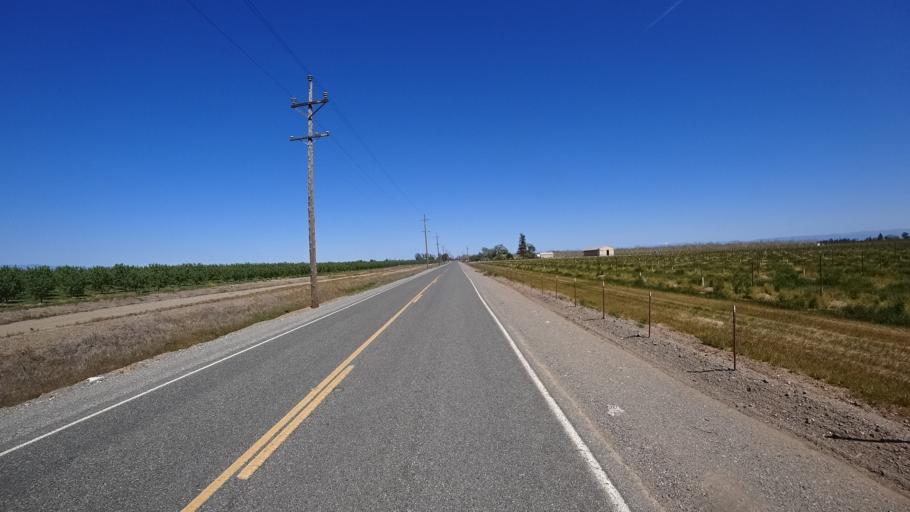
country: US
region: California
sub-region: Glenn County
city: Orland
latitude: 39.6832
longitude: -122.1781
